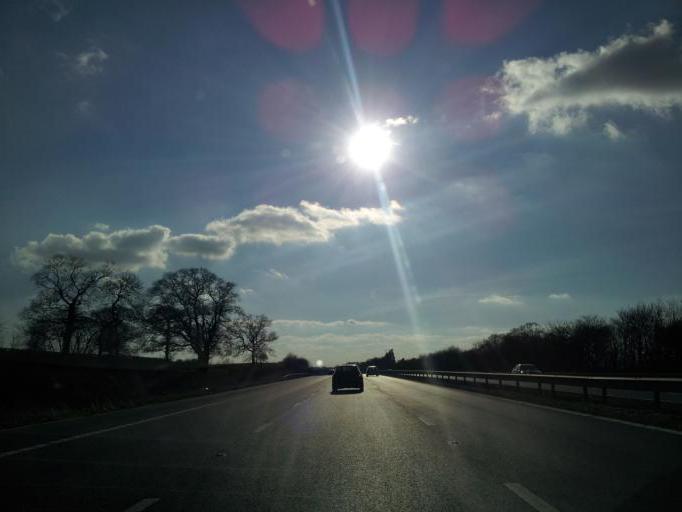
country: GB
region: England
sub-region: Devon
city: Uffculme
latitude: 50.9513
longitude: -3.2686
